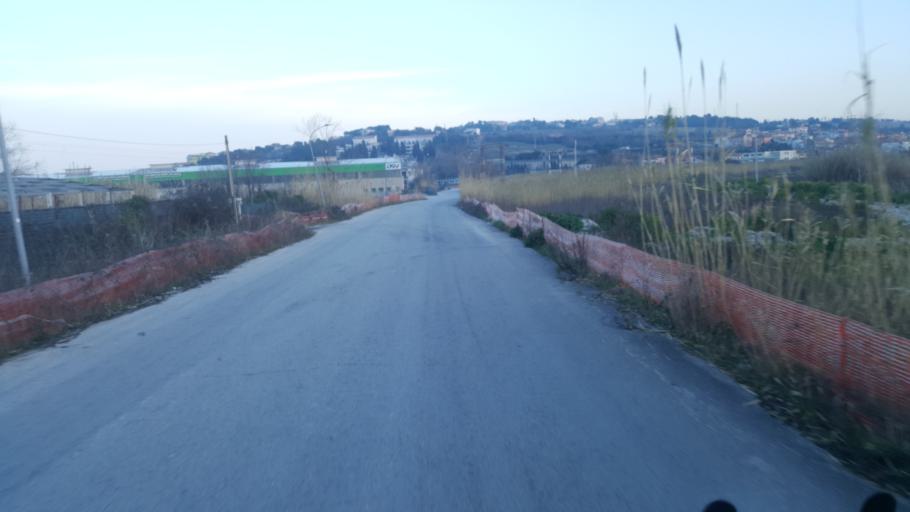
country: IT
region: The Marches
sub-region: Provincia di Ancona
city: Falconara Marittima
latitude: 43.6315
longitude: 13.3807
